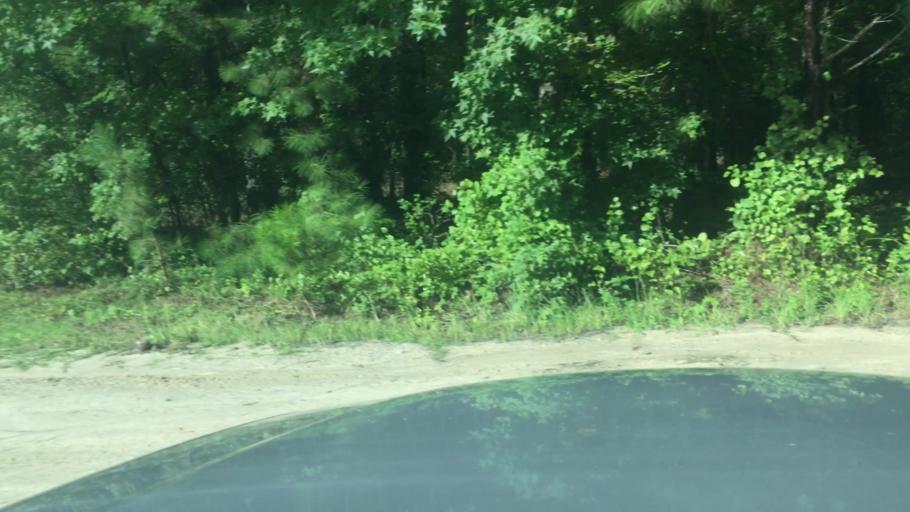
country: US
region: North Carolina
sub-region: Cumberland County
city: Eastover
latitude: 35.1567
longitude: -78.8531
